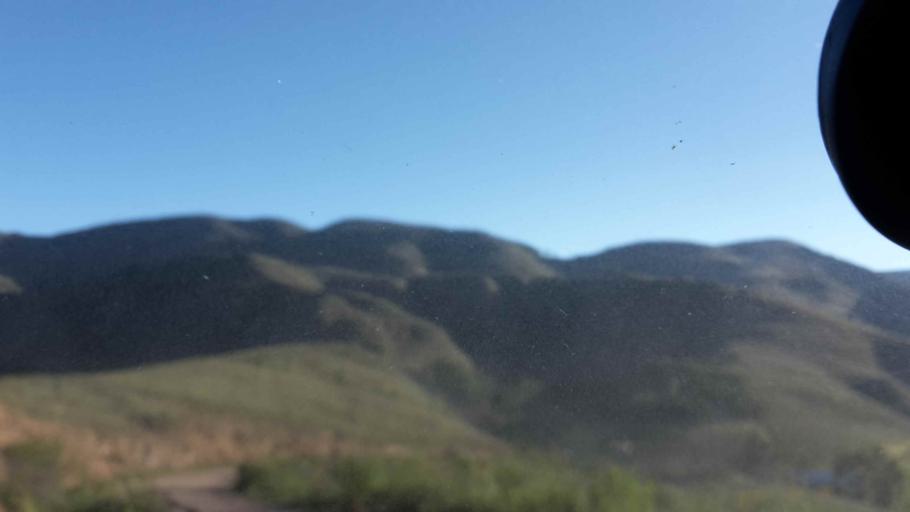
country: BO
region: Cochabamba
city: Arani
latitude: -17.7923
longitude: -65.5994
